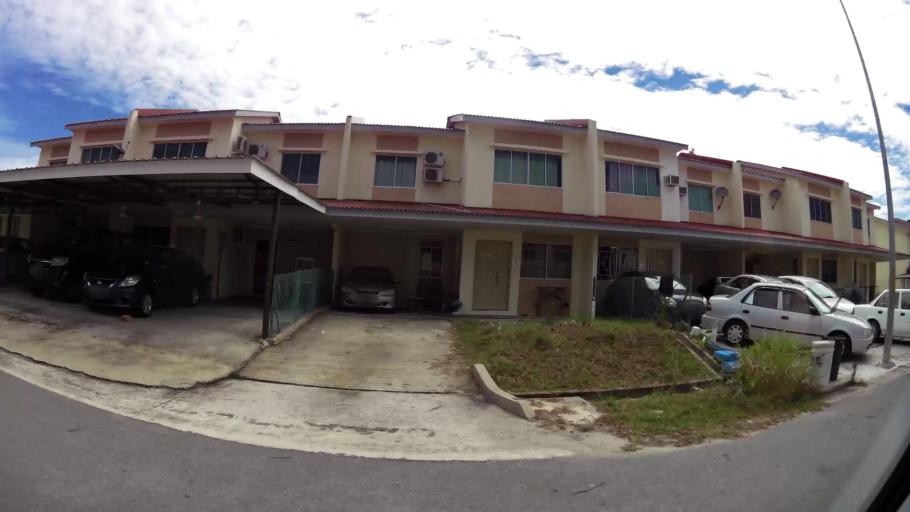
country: BN
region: Brunei and Muara
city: Bandar Seri Begawan
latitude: 4.9780
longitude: 115.0048
